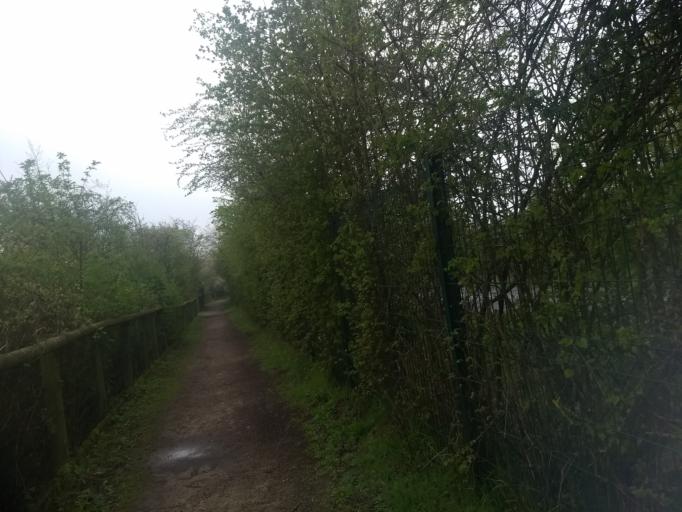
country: FR
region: Nord-Pas-de-Calais
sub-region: Departement du Pas-de-Calais
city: Roeux
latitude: 50.3016
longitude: 2.9151
